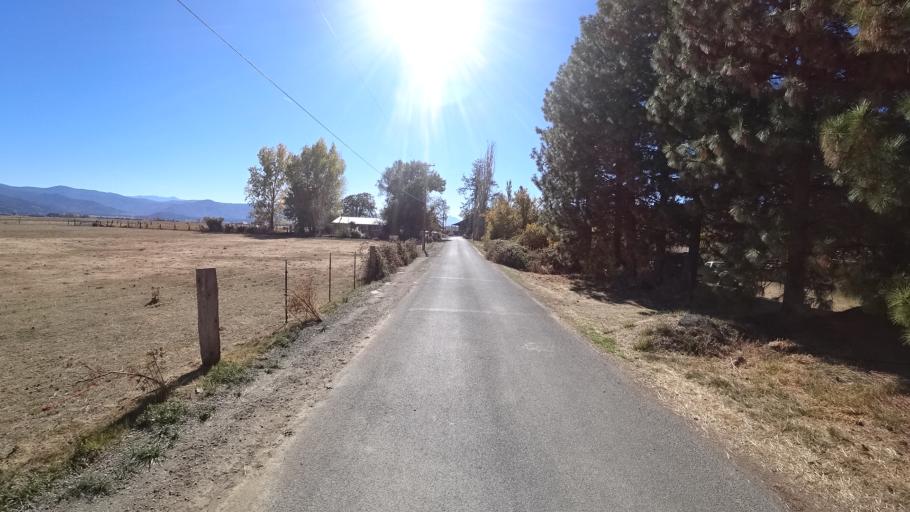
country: US
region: California
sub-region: Siskiyou County
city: Yreka
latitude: 41.5225
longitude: -122.9002
